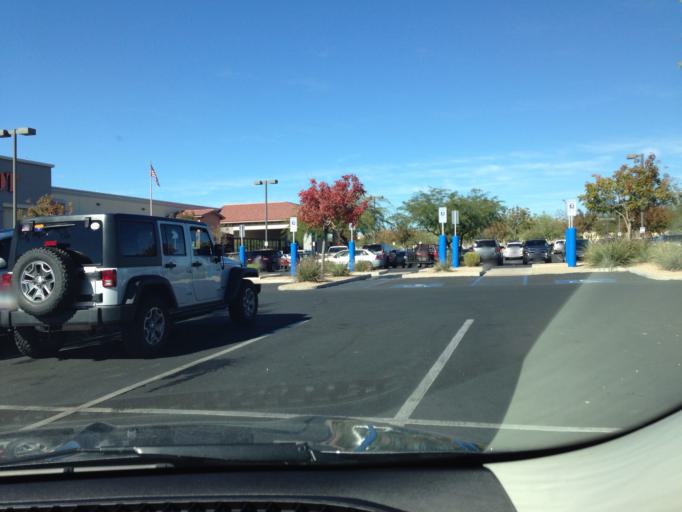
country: US
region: Arizona
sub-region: Maricopa County
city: Anthem
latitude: 33.8015
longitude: -112.1330
